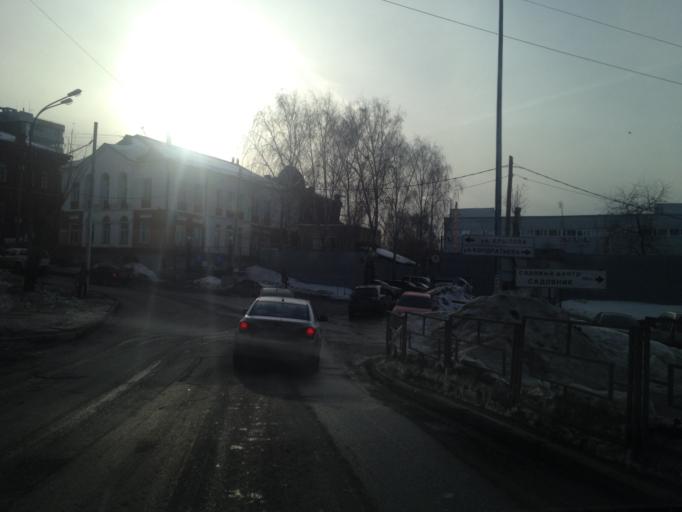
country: RU
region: Sverdlovsk
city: Yekaterinburg
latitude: 56.8419
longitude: 60.5714
